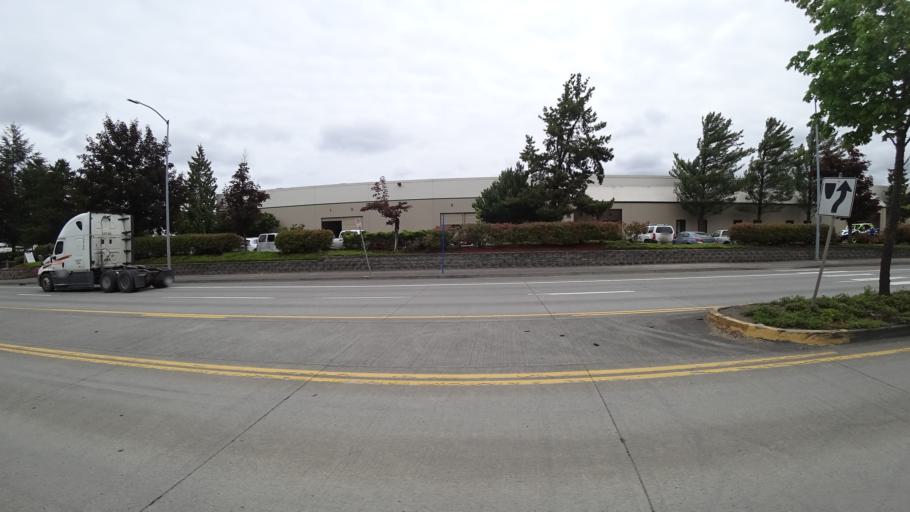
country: US
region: Washington
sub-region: Clark County
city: Vancouver
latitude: 45.6188
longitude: -122.7237
